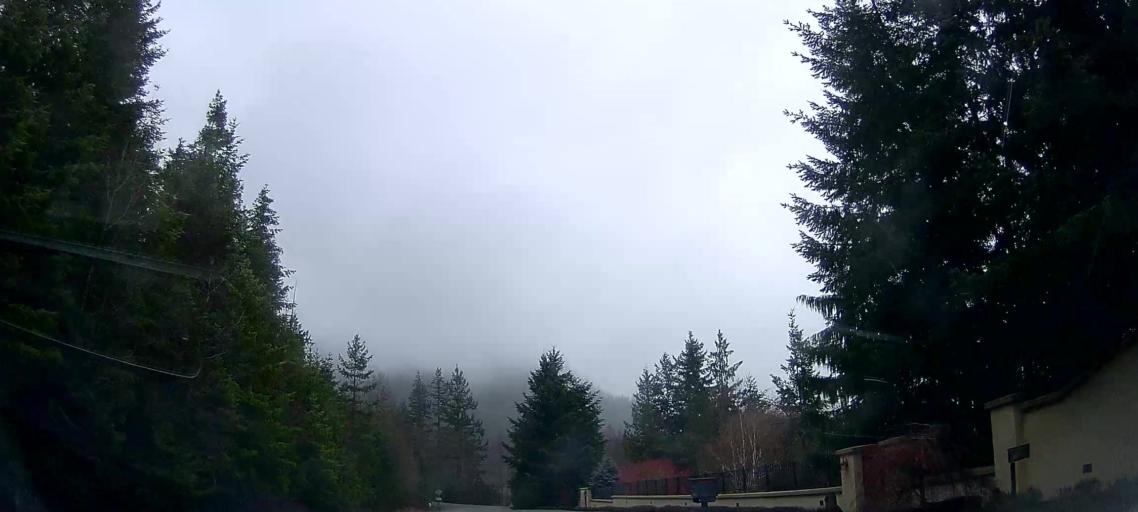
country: US
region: Washington
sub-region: Skagit County
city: Big Lake
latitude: 48.3790
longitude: -122.2922
